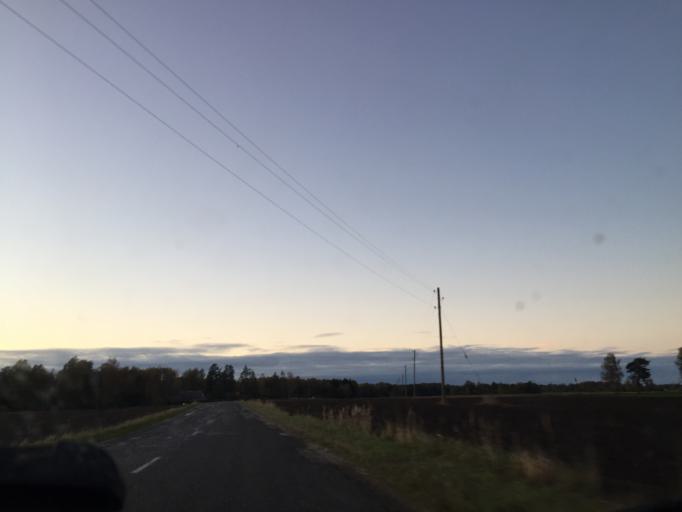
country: LV
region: Talsu Rajons
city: Sabile
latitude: 56.9650
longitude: 22.6087
